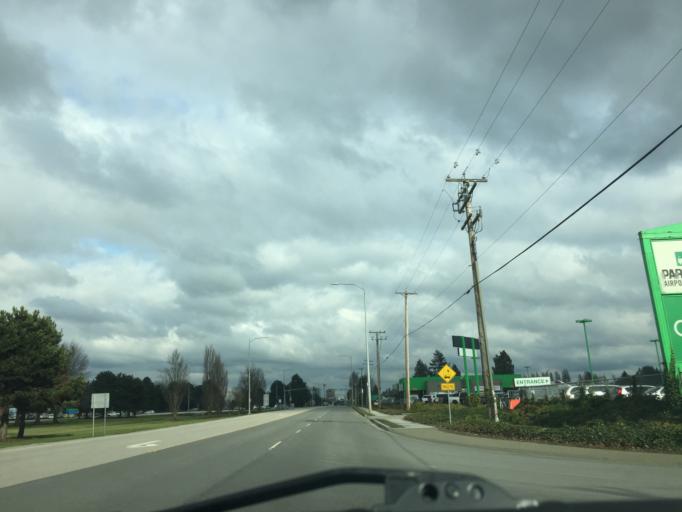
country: CA
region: British Columbia
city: Richmond
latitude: 49.1921
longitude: -123.1543
